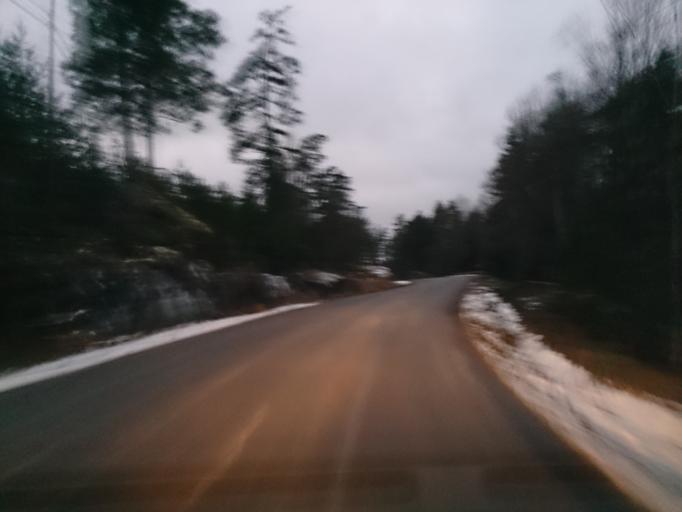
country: SE
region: OEstergoetland
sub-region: Atvidabergs Kommun
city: Atvidaberg
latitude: 58.2267
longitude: 16.0613
